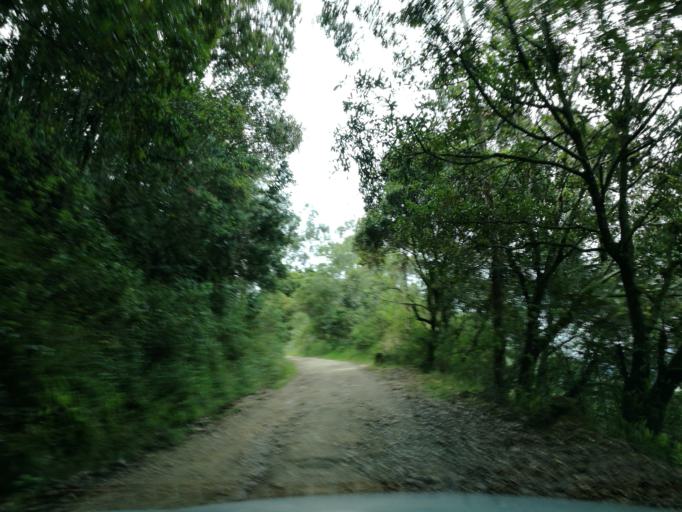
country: CO
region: Boyaca
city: Arcabuco
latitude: 5.7543
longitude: -73.4522
